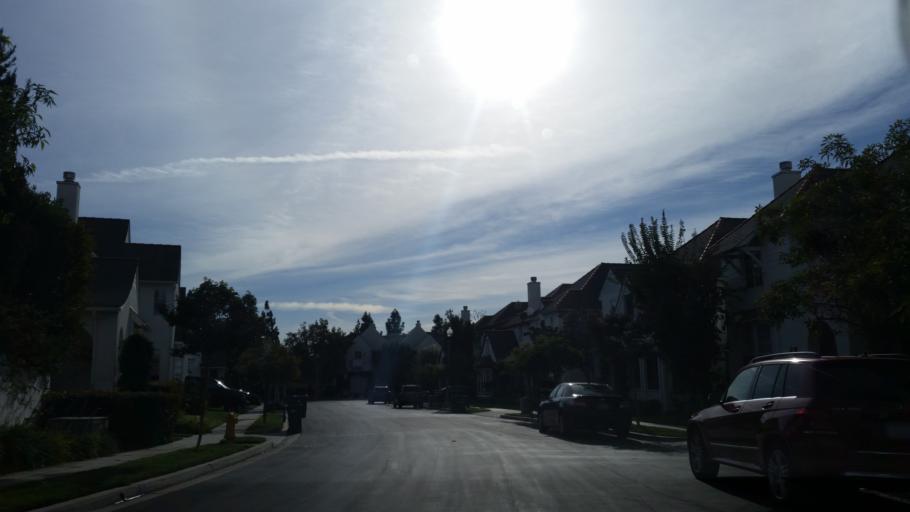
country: US
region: California
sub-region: Orange County
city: North Tustin
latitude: 33.7293
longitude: -117.7563
